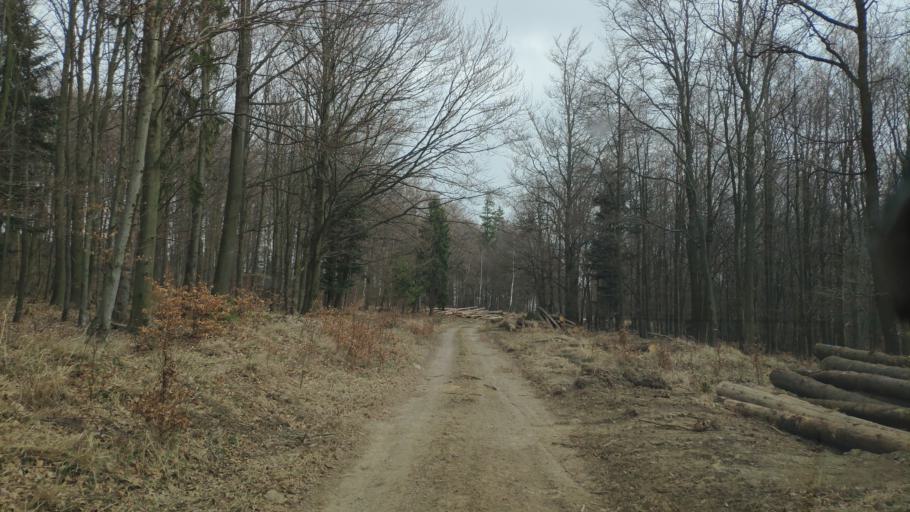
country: SK
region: Kosicky
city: Moldava nad Bodvou
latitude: 48.7432
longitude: 21.0437
